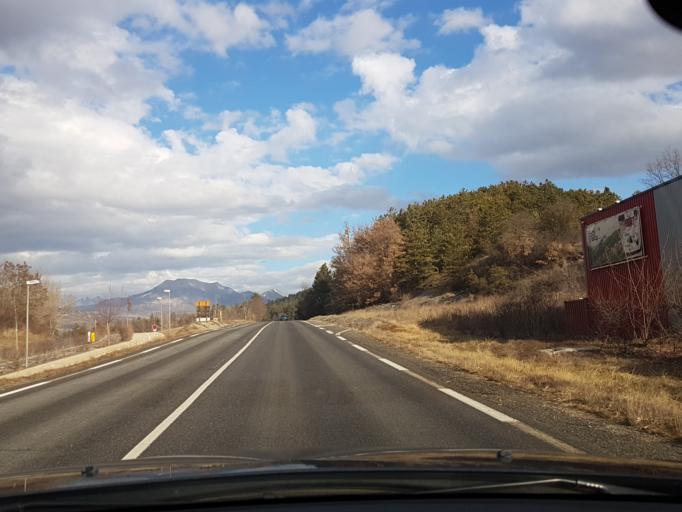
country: FR
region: Provence-Alpes-Cote d'Azur
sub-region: Departement des Hautes-Alpes
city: Tallard
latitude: 44.4603
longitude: 6.0338
